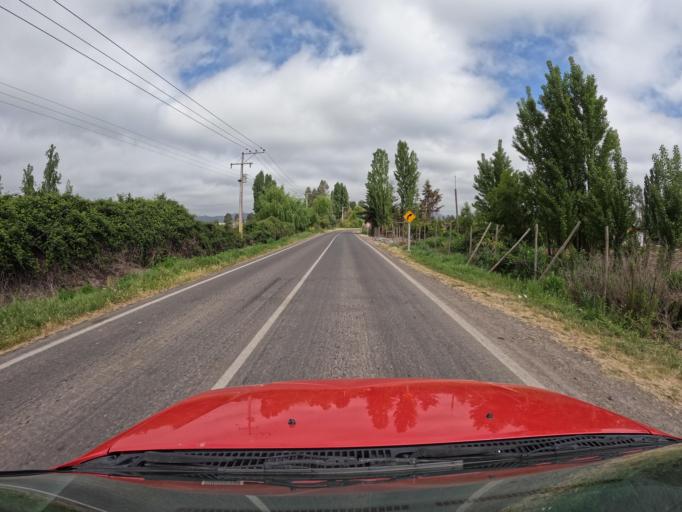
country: CL
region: O'Higgins
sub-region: Provincia de Colchagua
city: Santa Cruz
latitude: -34.6781
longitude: -71.3612
